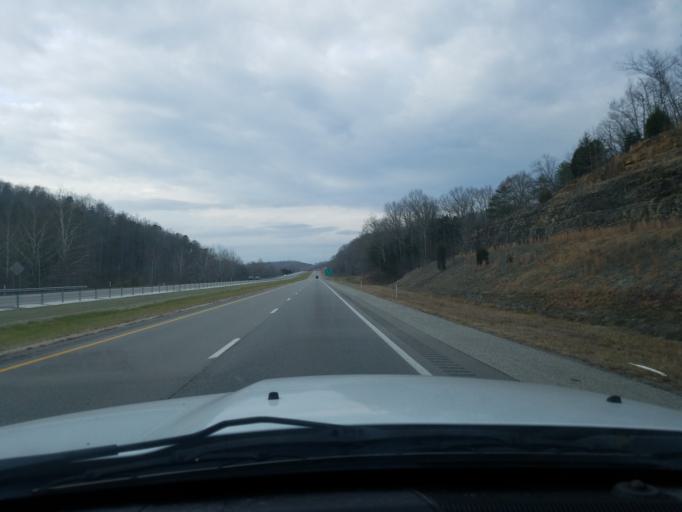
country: US
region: Kentucky
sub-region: Carter County
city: Olive Hill
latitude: 38.3268
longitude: -83.1822
